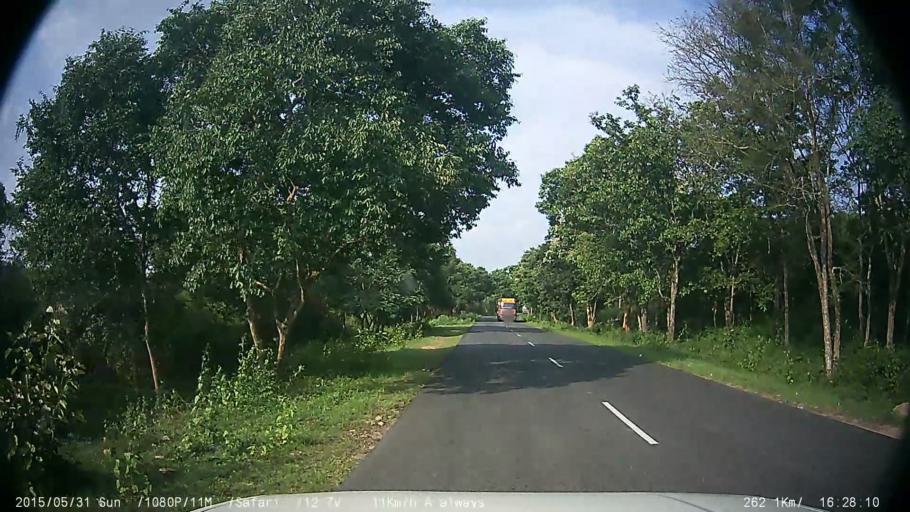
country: IN
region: Karnataka
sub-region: Chamrajnagar
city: Gundlupet
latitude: 11.7684
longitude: 76.5397
